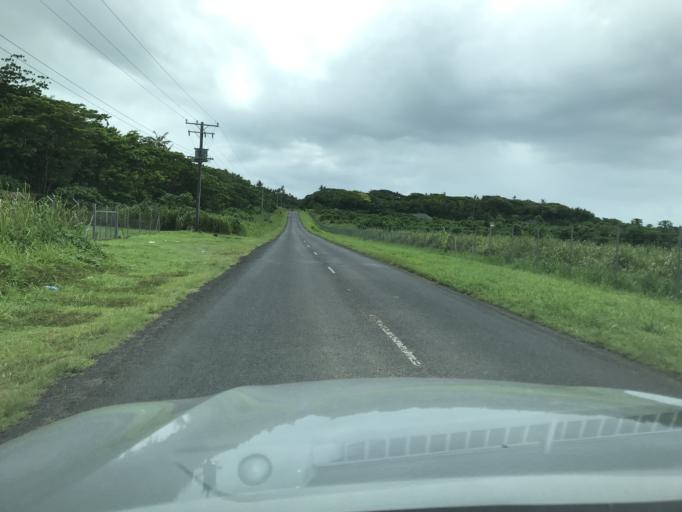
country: WS
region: Aiga-i-le-Tai
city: Mulifanua
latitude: -13.8339
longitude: -172.0115
